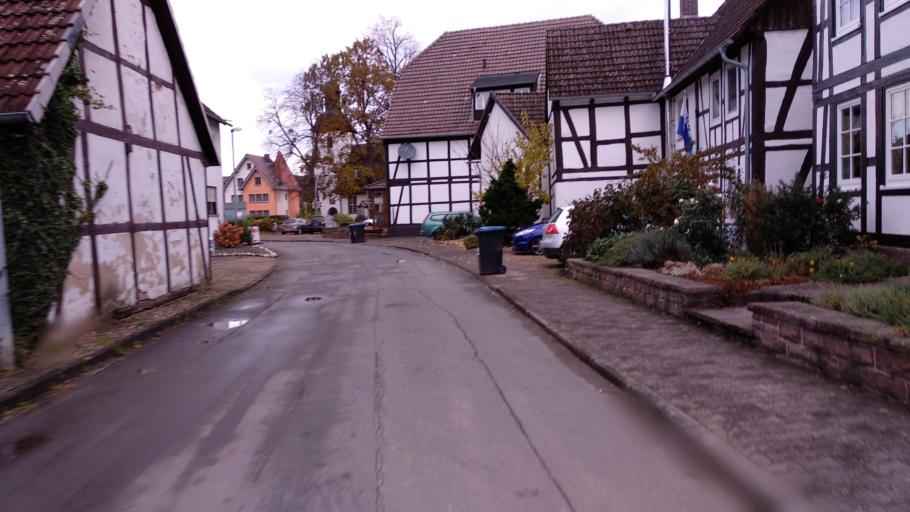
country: DE
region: North Rhine-Westphalia
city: Beverungen
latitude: 51.6605
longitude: 9.3821
